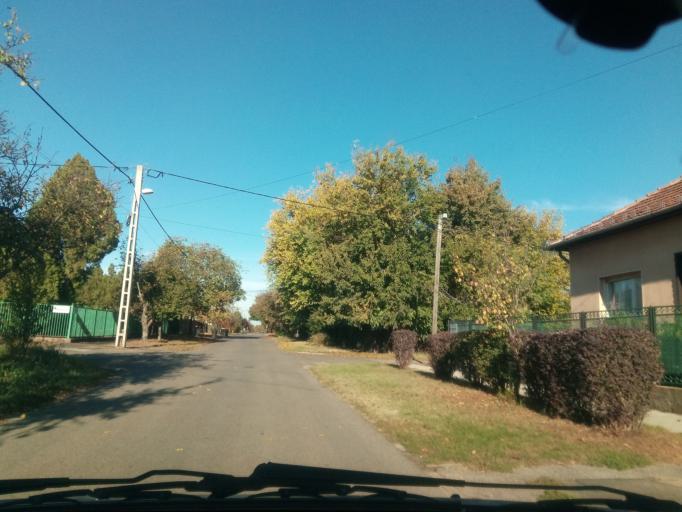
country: HU
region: Budapest
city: Budapest XVIII. keruelet
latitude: 47.4349
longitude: 19.2173
